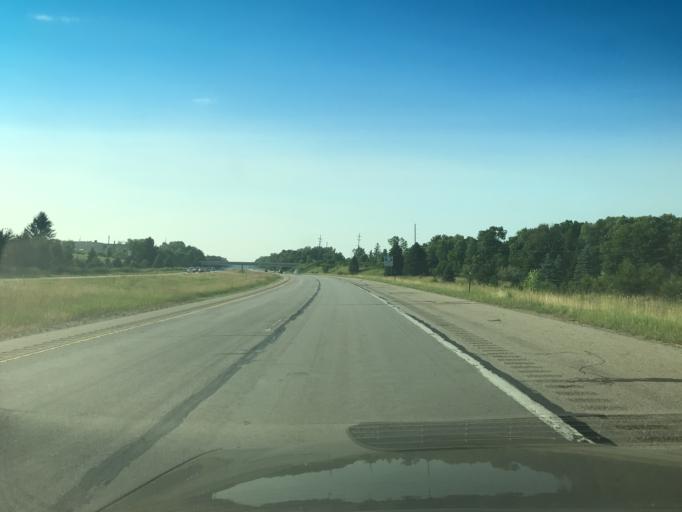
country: US
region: Michigan
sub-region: Ingham County
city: Mason
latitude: 42.5928
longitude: -84.4633
